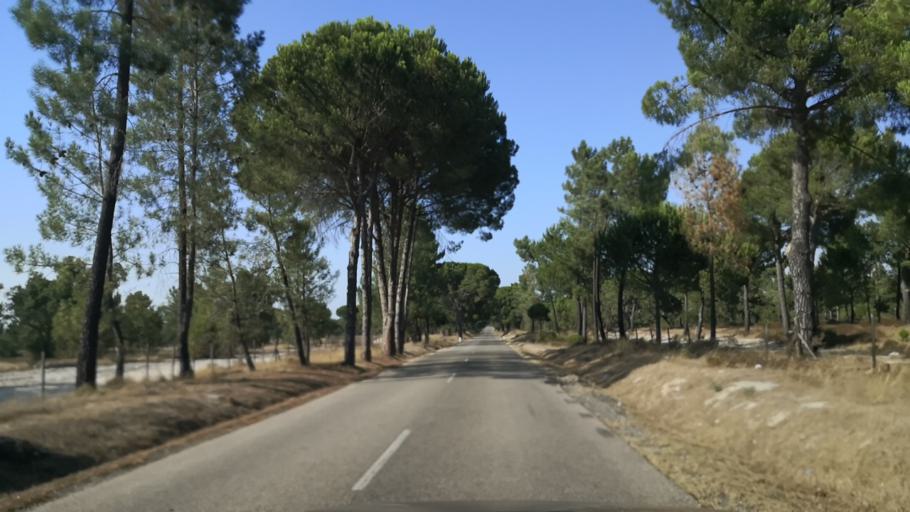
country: PT
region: Santarem
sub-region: Coruche
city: Coruche
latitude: 38.9069
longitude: -8.5271
